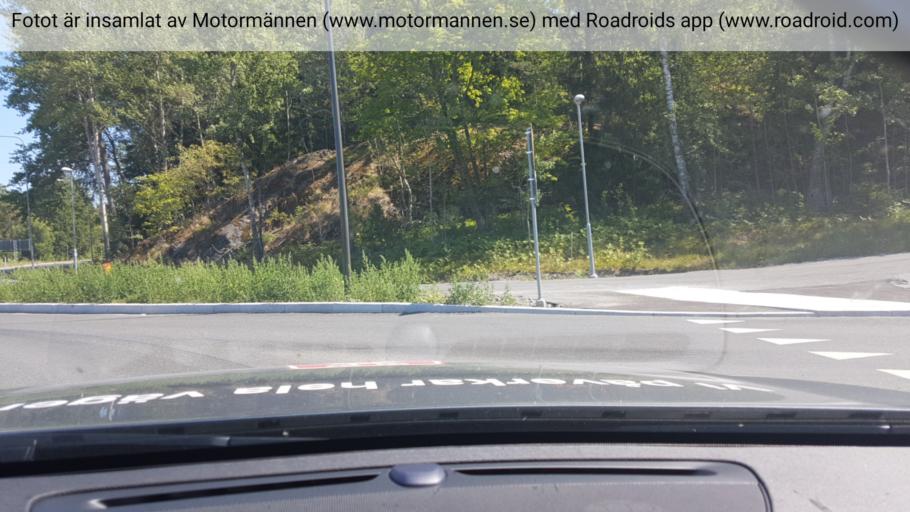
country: SE
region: Stockholm
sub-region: Haninge Kommun
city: Haninge
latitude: 59.1869
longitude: 18.1561
